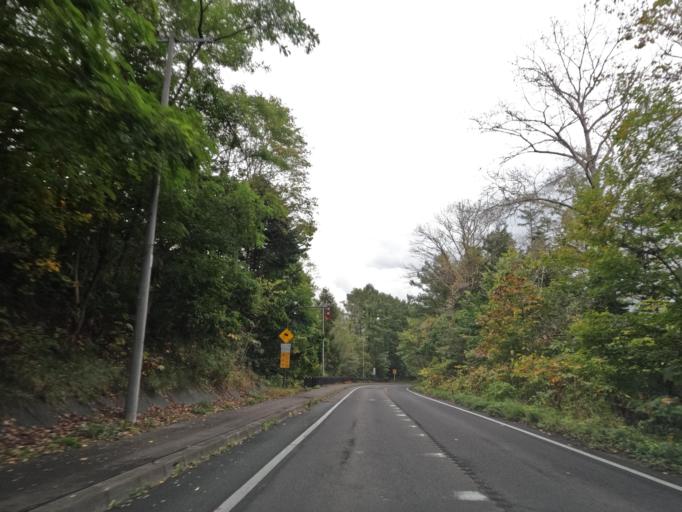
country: JP
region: Hokkaido
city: Date
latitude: 42.5377
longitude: 140.8597
